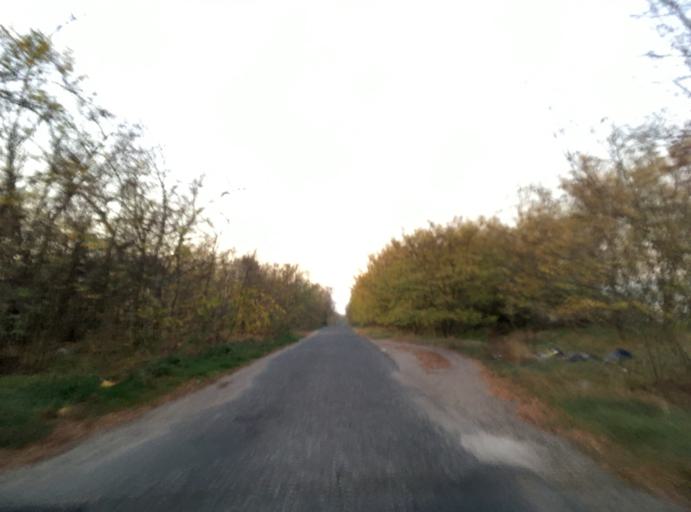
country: HU
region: Komarom-Esztergom
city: Acs
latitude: 47.7203
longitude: 18.0208
